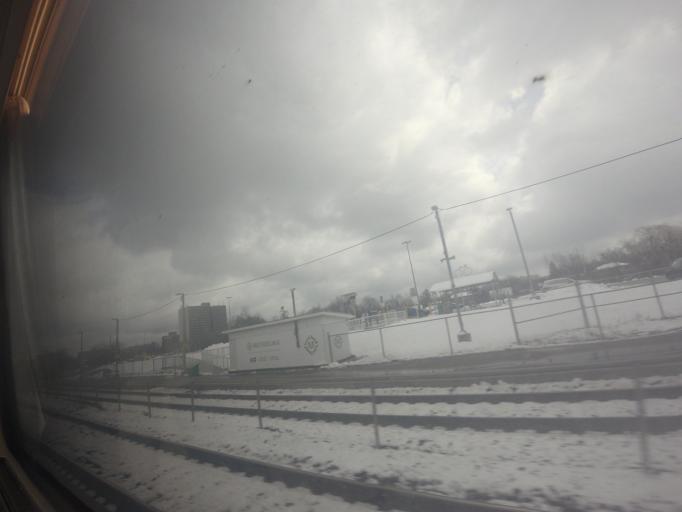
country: CA
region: Ontario
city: Scarborough
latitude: 43.7400
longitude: -79.2316
